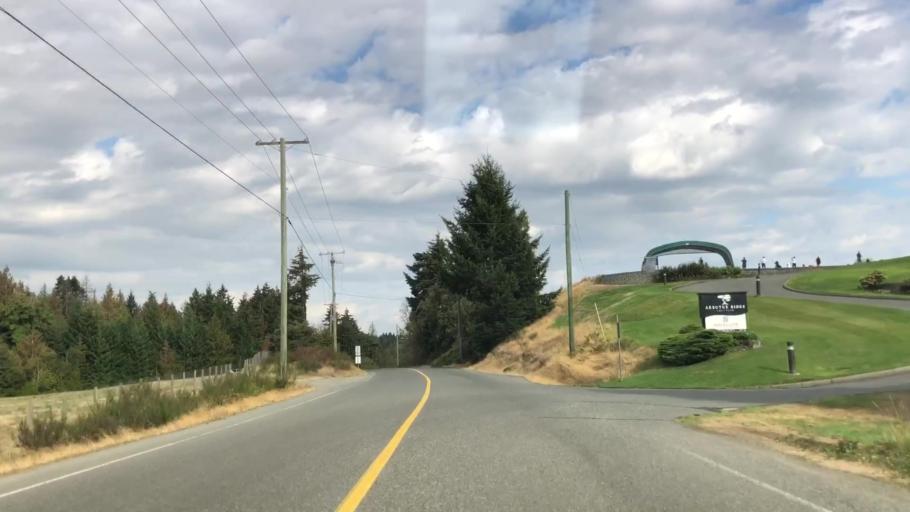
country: CA
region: British Columbia
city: North Saanich
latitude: 48.6869
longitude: -123.5534
